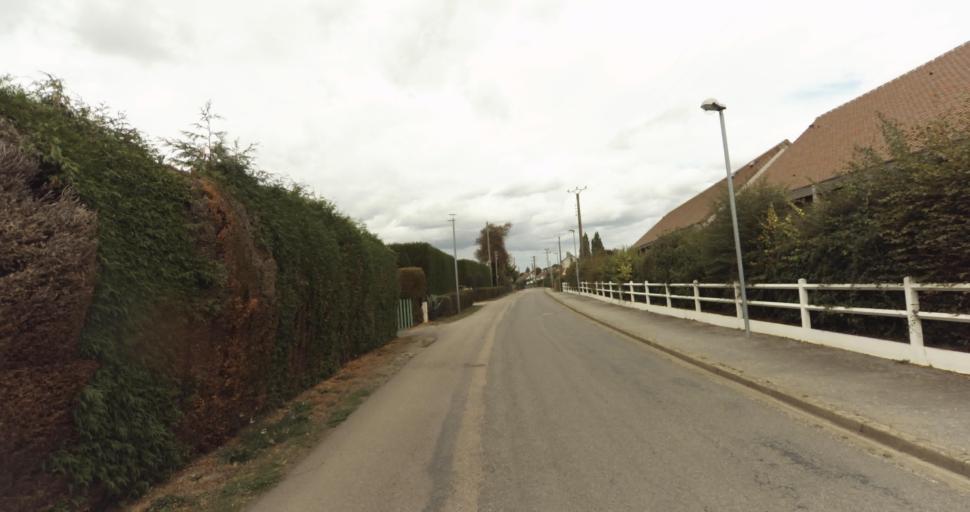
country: FR
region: Lower Normandy
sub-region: Departement de l'Orne
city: Gace
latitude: 48.8889
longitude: 0.3395
